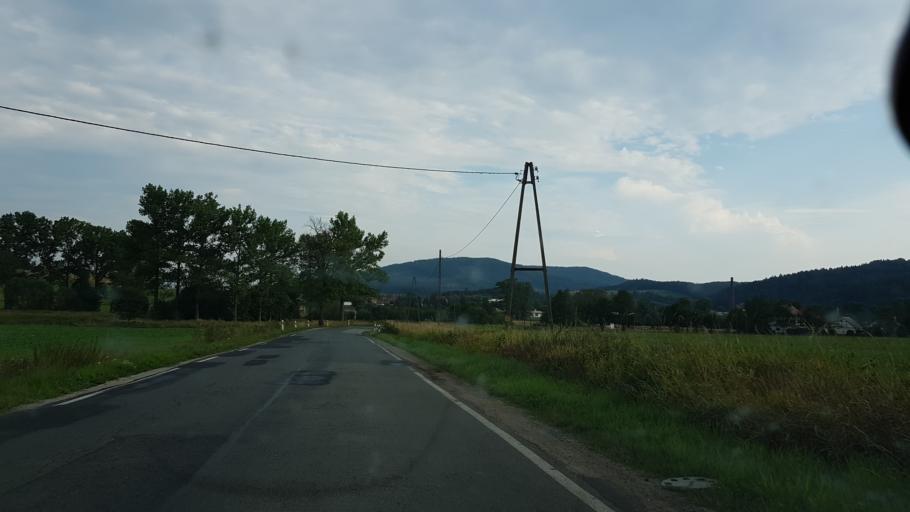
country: PL
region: Lower Silesian Voivodeship
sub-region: Powiat kamiennogorski
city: Marciszow
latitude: 50.8600
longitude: 16.0025
